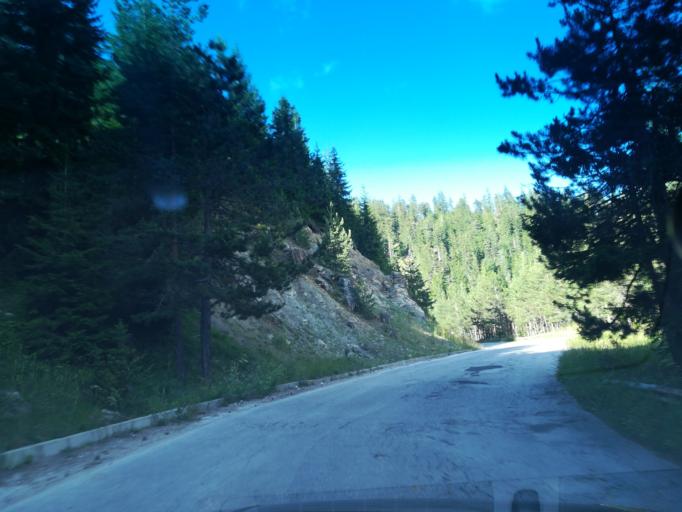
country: BG
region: Smolyan
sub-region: Obshtina Chepelare
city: Chepelare
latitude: 41.6869
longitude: 24.7527
